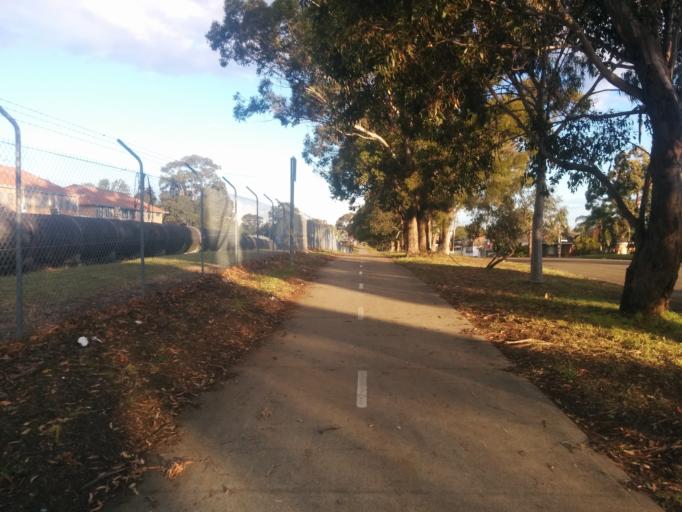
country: AU
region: New South Wales
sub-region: Holroyd
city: Guildford West
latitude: -33.8546
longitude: 150.9792
